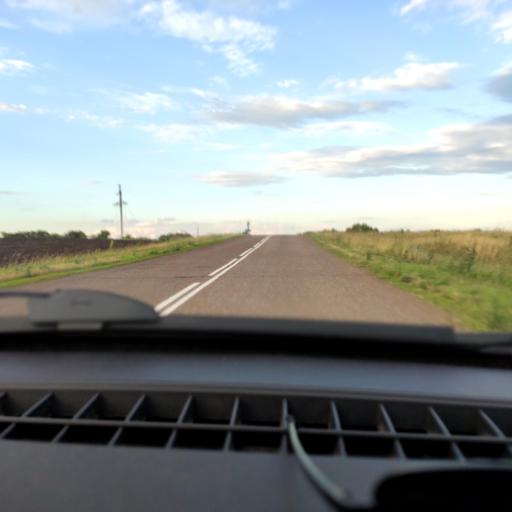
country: RU
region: Bashkortostan
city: Chishmy
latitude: 54.3926
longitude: 55.5325
